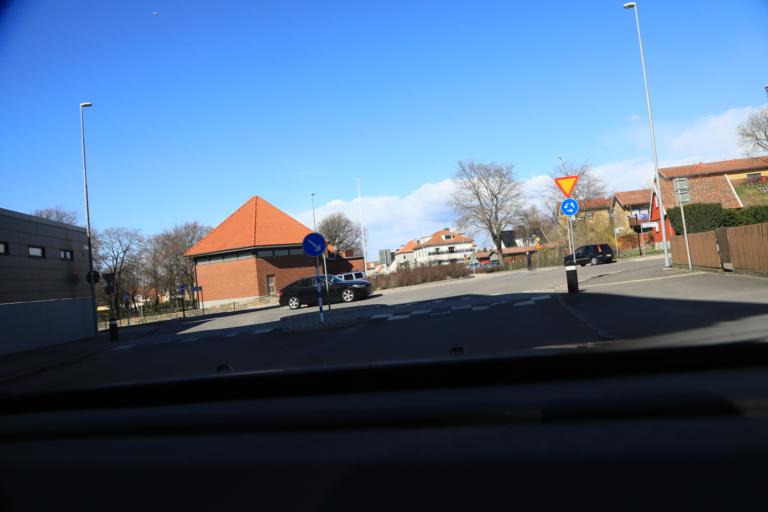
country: SE
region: Halland
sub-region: Varbergs Kommun
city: Varberg
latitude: 57.1044
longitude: 12.2558
